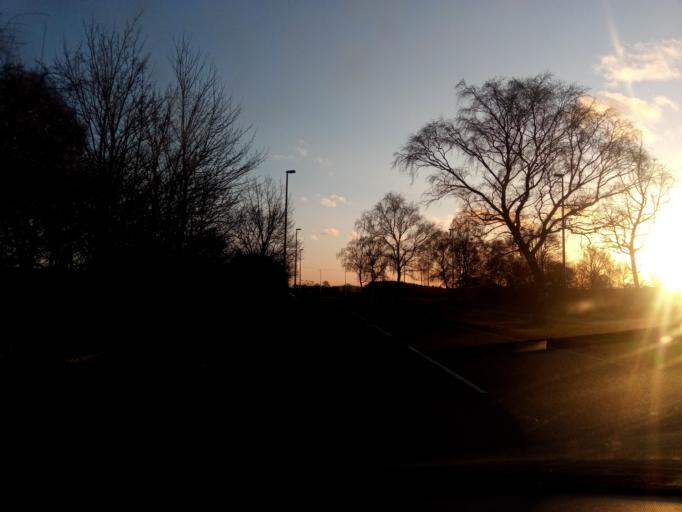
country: GB
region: England
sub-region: Nottinghamshire
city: Farnsfield
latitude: 53.0689
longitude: -1.0704
